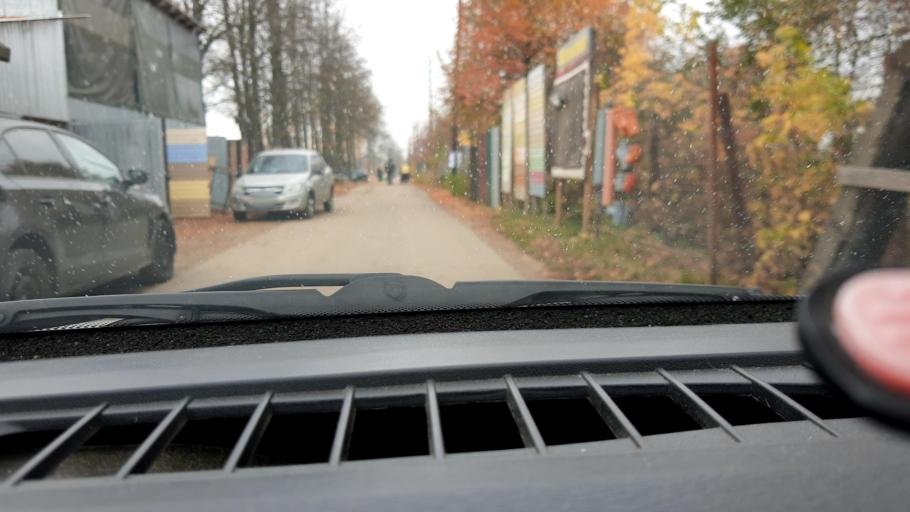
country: RU
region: Nizjnij Novgorod
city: Gorbatovka
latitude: 56.2590
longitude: 43.8398
